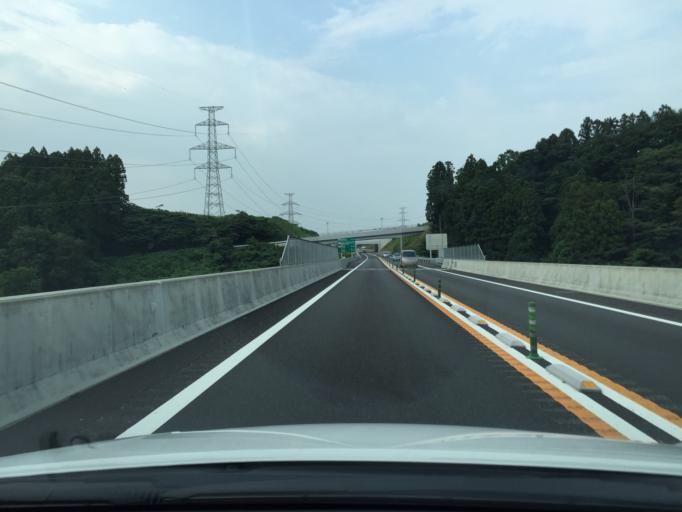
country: JP
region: Fukushima
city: Namie
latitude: 37.5094
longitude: 140.9430
